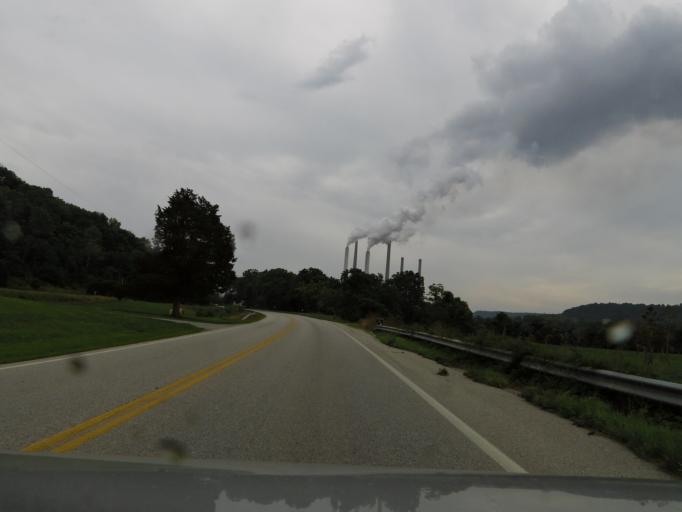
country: US
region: Ohio
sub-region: Brown County
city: Ripley
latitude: 38.7134
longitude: -83.8231
